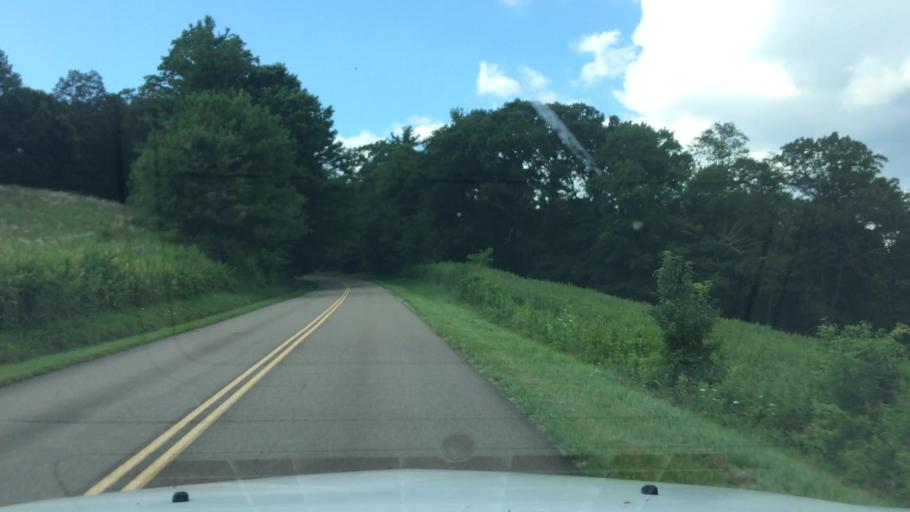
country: US
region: North Carolina
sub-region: Watauga County
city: Blowing Rock
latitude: 36.1529
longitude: -81.6670
